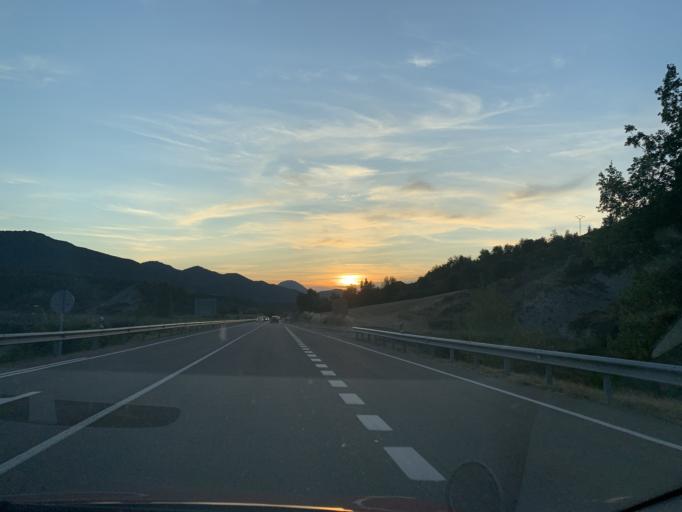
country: ES
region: Aragon
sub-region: Provincia de Huesca
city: Yebra de Basa
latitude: 42.4783
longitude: -0.2641
